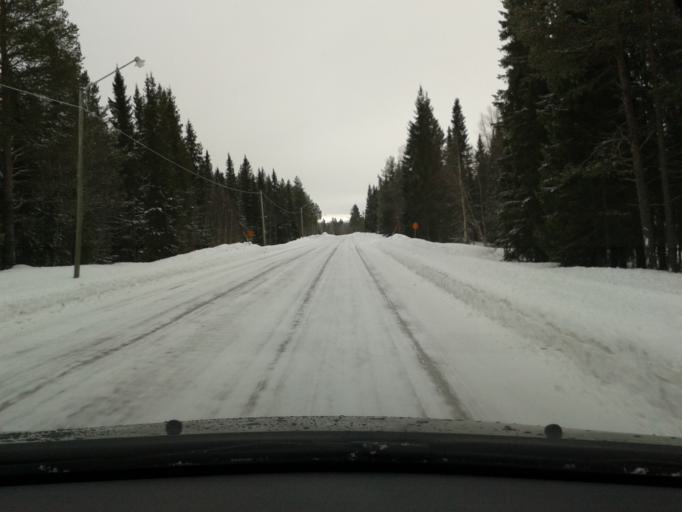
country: SE
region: Vaesterbotten
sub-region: Vilhelmina Kommun
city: Sjoberg
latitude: 64.8390
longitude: 15.9217
